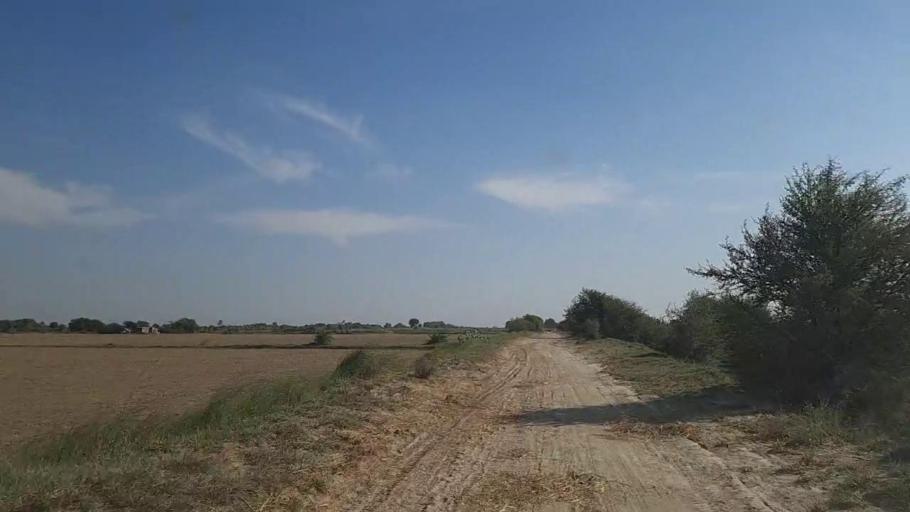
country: PK
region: Sindh
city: Bulri
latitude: 24.8629
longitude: 68.2853
